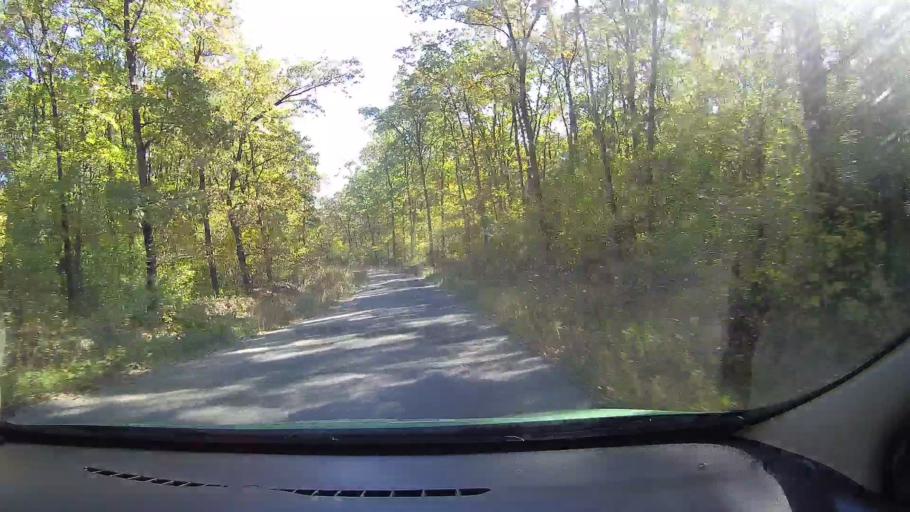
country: RO
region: Satu Mare
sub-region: Comuna Terebesti
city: Terebesti
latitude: 47.7080
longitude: 22.7563
